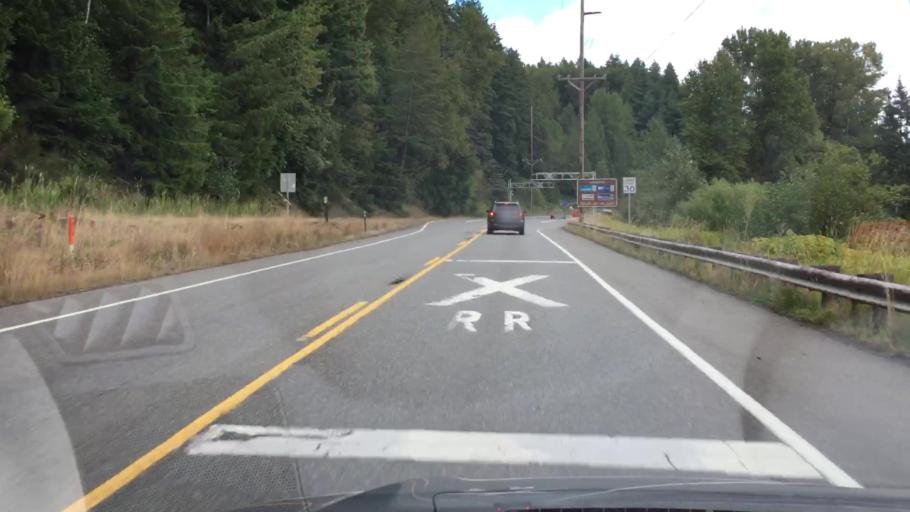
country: US
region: Washington
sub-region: Pierce County
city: Eatonville
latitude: 46.7685
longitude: -122.1991
